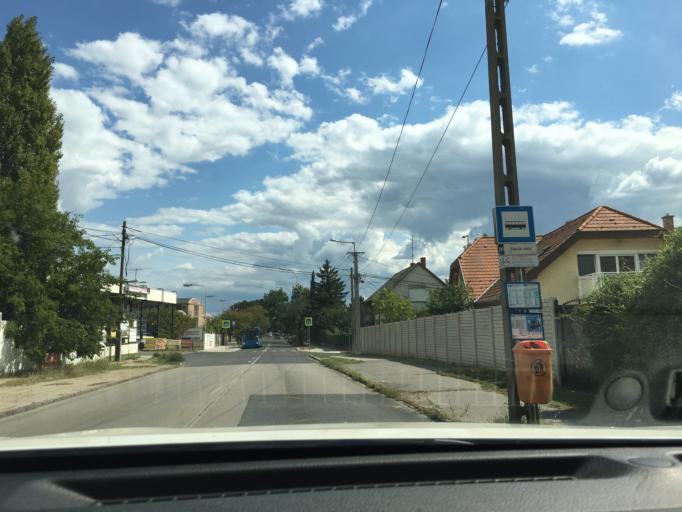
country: HU
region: Budapest
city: Budapest XVI. keruelet
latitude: 47.5205
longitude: 19.1875
